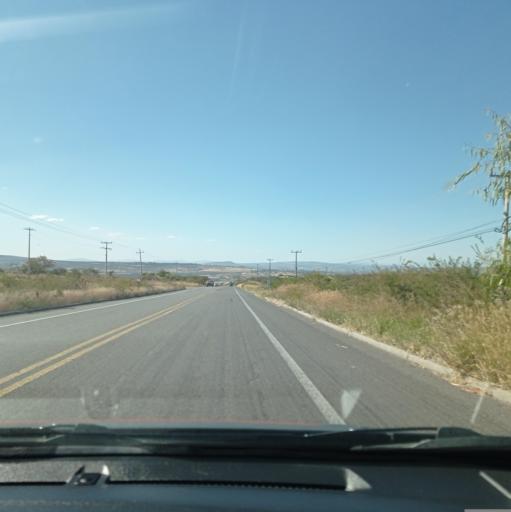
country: MX
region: Jalisco
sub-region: San Julian
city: Colonia Veintitres de Mayo
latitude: 21.0087
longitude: -102.2586
